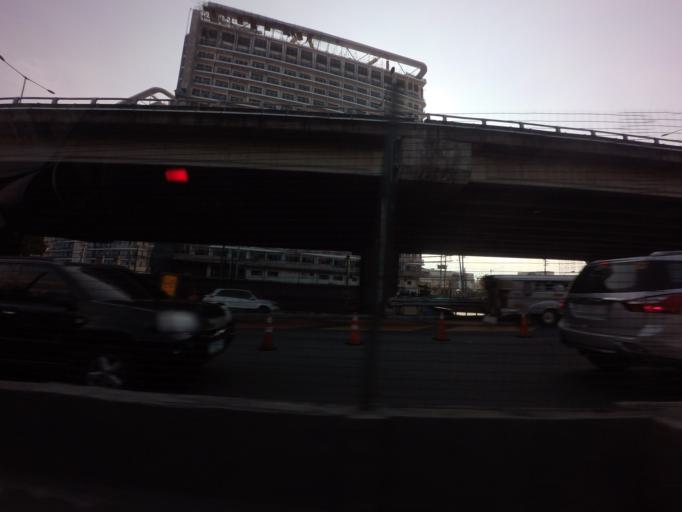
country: PH
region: Calabarzon
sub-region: Province of Rizal
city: Taguig
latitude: 14.4853
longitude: 121.0454
